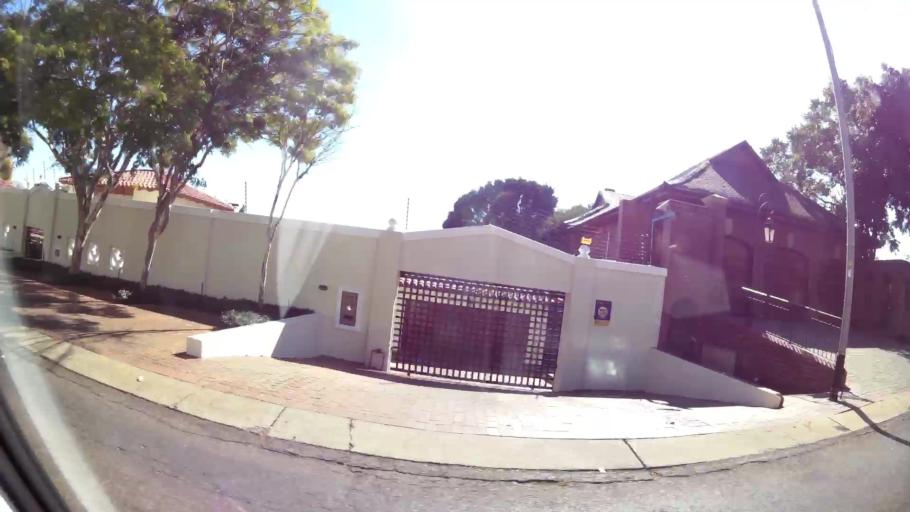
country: ZA
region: Gauteng
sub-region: City of Tshwane Metropolitan Municipality
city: Pretoria
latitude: -25.7819
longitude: 28.2339
